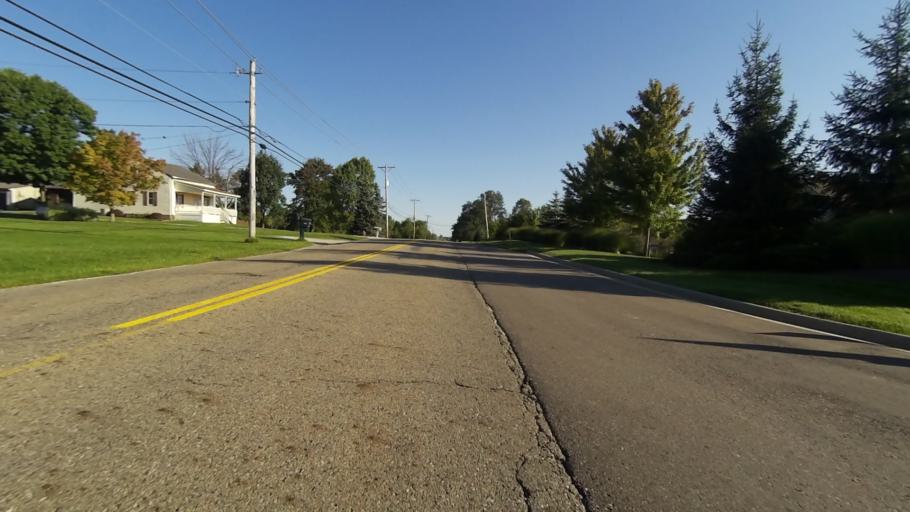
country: US
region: Ohio
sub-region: Portage County
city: Streetsboro
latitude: 41.2557
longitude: -81.3266
